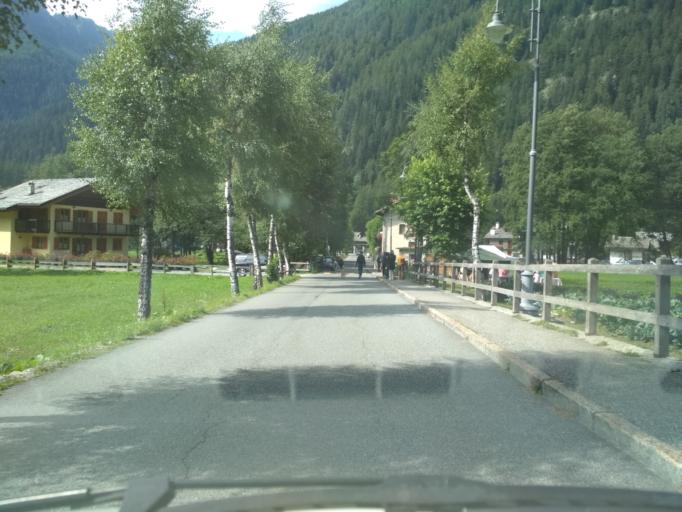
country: IT
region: Aosta Valley
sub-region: Valle d'Aosta
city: Gressoney-Saint-Jean
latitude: 45.7714
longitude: 7.8287
